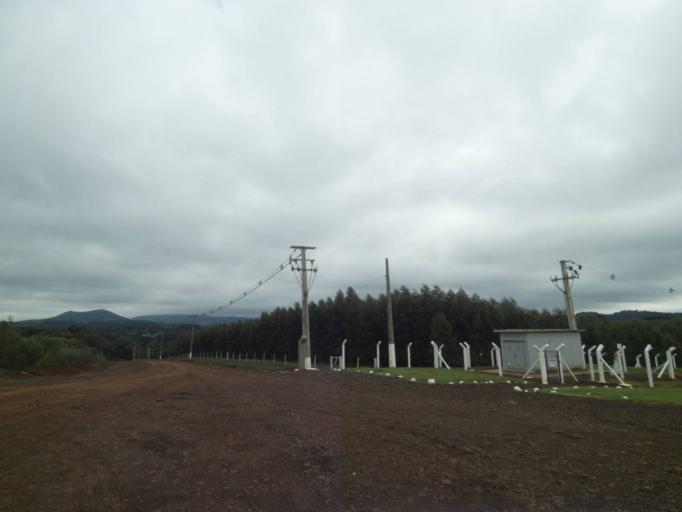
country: BR
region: Parana
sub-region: Pitanga
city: Pitanga
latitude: -24.9436
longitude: -51.8795
